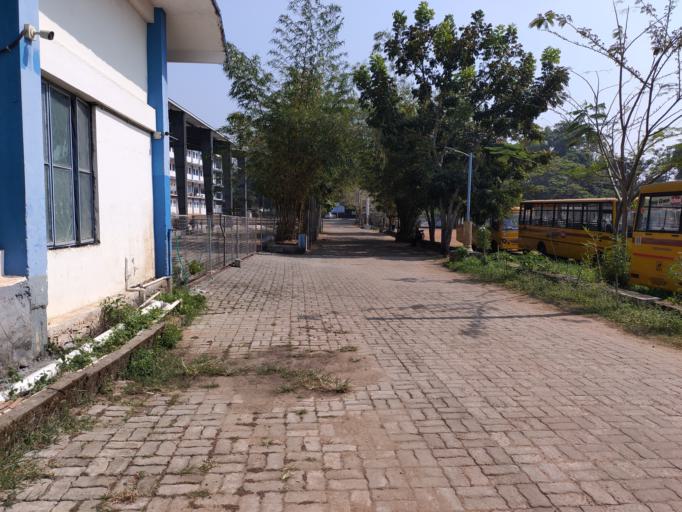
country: IN
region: Kerala
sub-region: Thrissur District
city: Kodungallur
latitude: 10.2330
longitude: 76.2771
